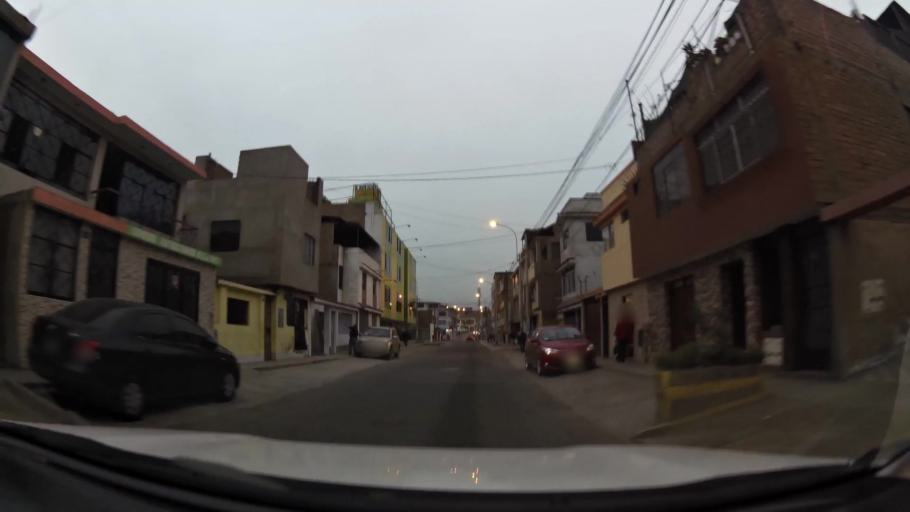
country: PE
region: Lima
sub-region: Lima
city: Surco
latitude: -12.1673
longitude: -76.9701
